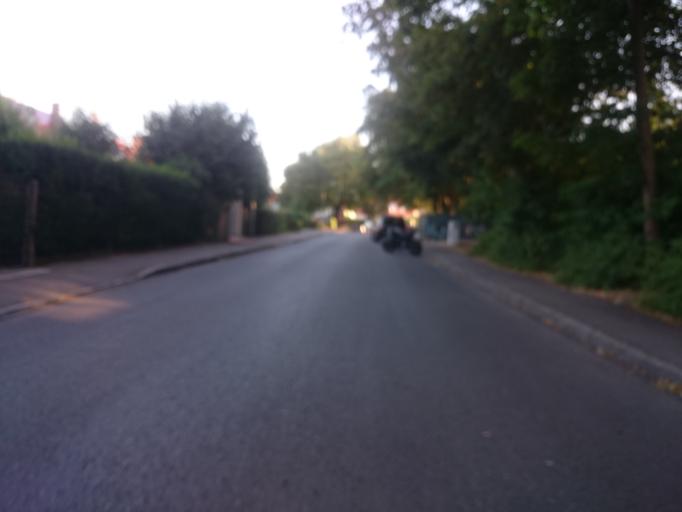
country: DE
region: Bavaria
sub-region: Swabia
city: Konigsbrunn
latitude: 48.3056
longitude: 10.8977
